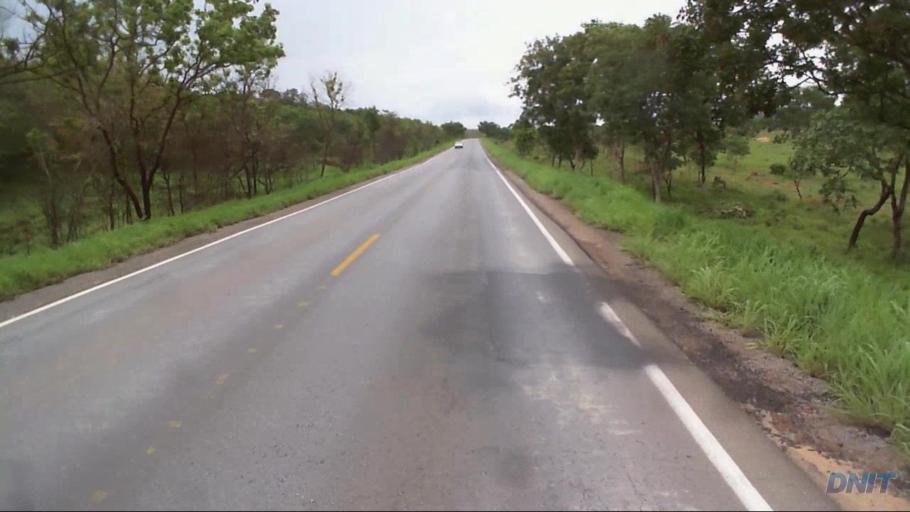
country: BR
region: Goias
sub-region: Padre Bernardo
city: Padre Bernardo
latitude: -15.4528
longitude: -48.2107
